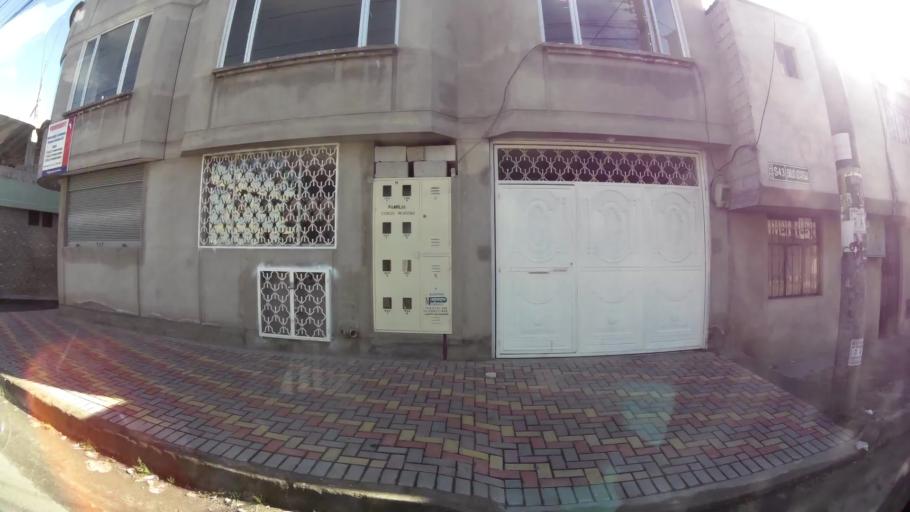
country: EC
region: Pichincha
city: Quito
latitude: -0.3044
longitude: -78.5663
